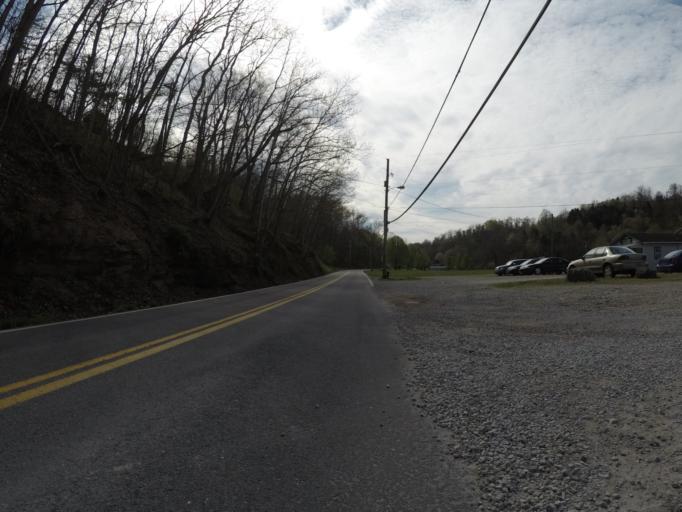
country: US
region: West Virginia
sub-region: Cabell County
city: Pea Ridge
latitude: 38.3810
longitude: -82.3755
